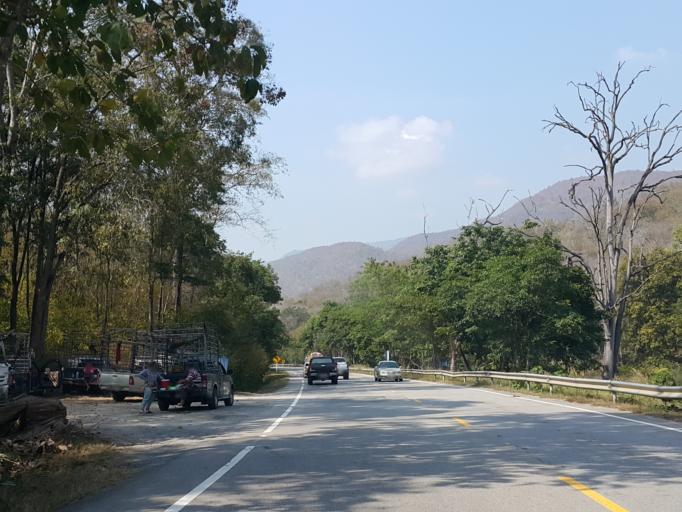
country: TH
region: Chiang Mai
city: Hot
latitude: 18.2340
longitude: 98.5480
